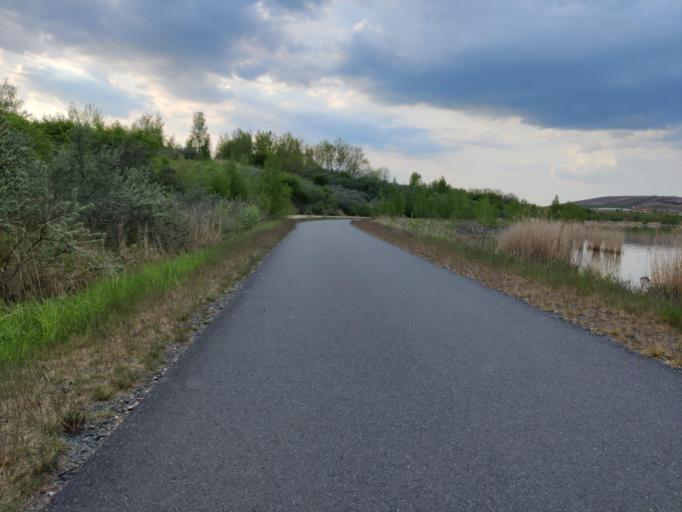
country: DE
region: Saxony
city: Rotha
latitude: 51.2254
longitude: 12.4279
